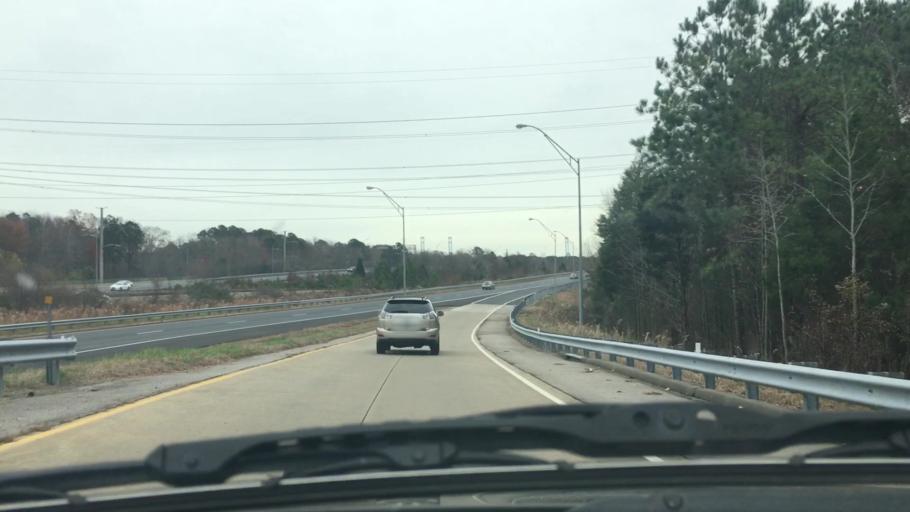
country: US
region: Virginia
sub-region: City of Portsmouth
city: Portsmouth Heights
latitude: 36.8721
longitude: -76.3760
